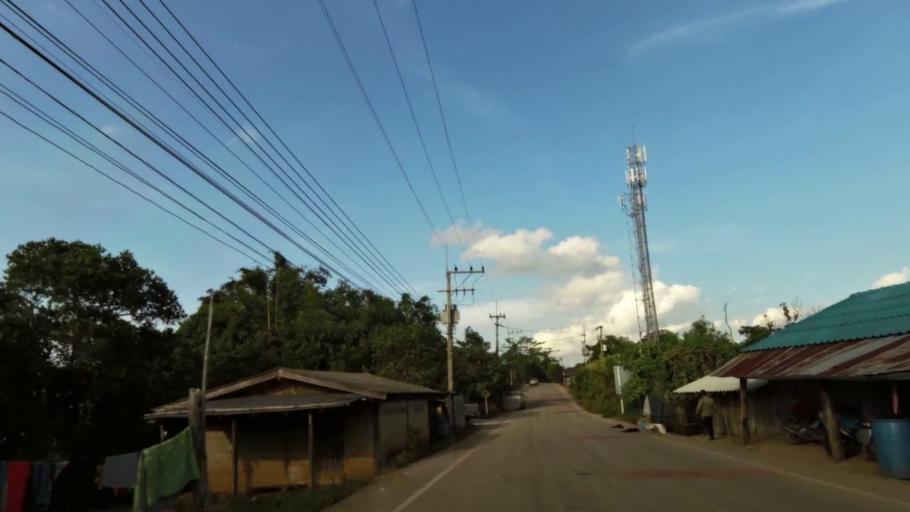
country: TH
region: Chiang Rai
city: Khun Tan
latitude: 19.8693
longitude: 100.3396
